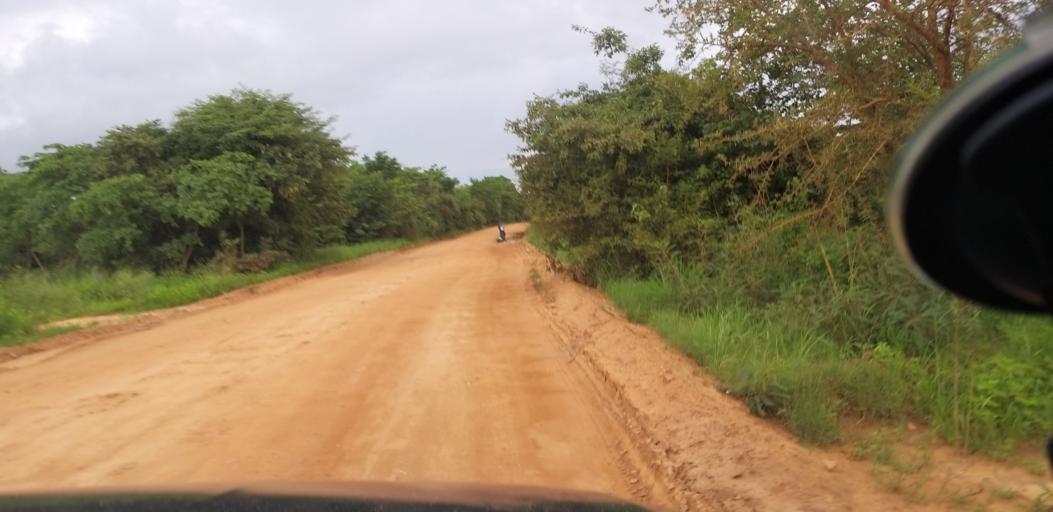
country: ZM
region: Lusaka
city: Lusaka
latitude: -15.1900
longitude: 28.4452
